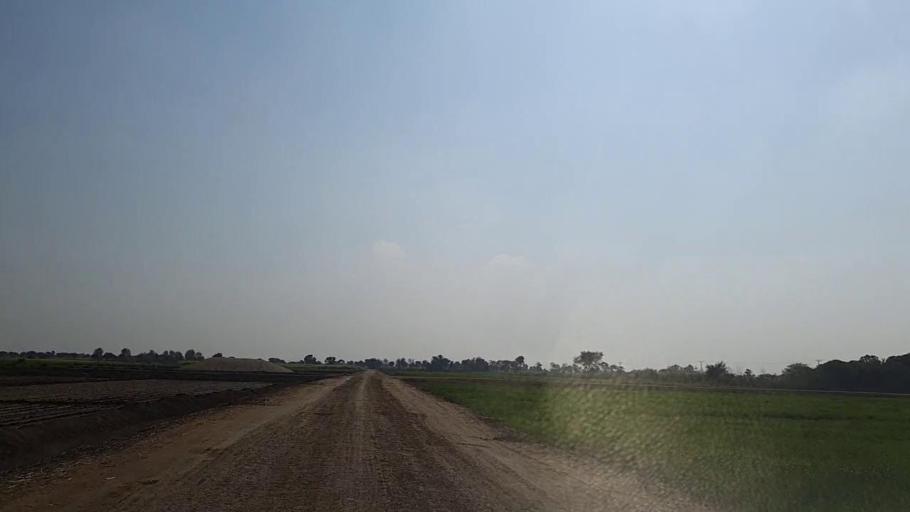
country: PK
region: Sindh
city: Daur
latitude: 26.4428
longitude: 68.2332
